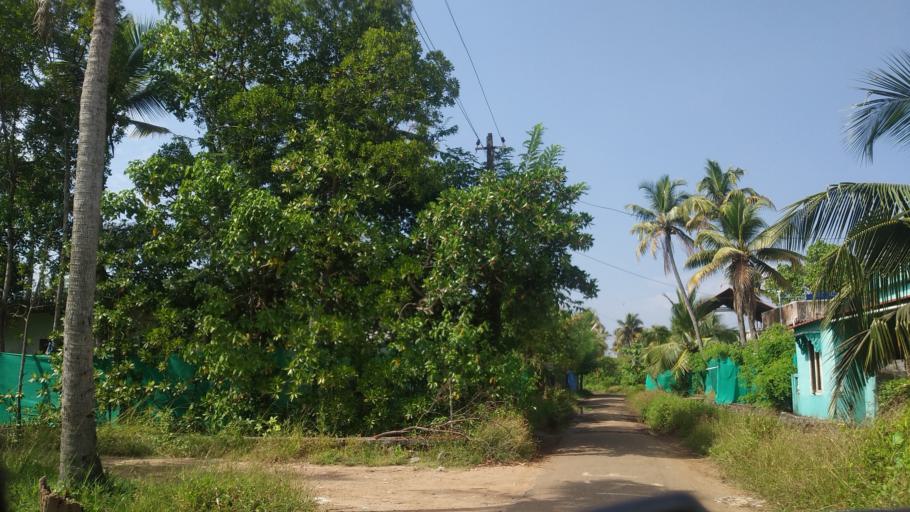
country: IN
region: Kerala
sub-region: Ernakulam
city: Elur
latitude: 10.0816
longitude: 76.2032
